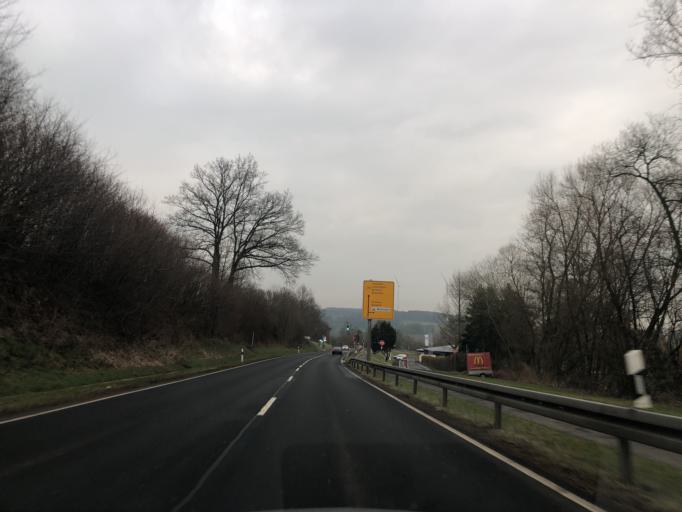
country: DE
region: Hesse
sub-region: Regierungsbezirk Darmstadt
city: Wachtersbach
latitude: 50.2633
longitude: 9.3059
